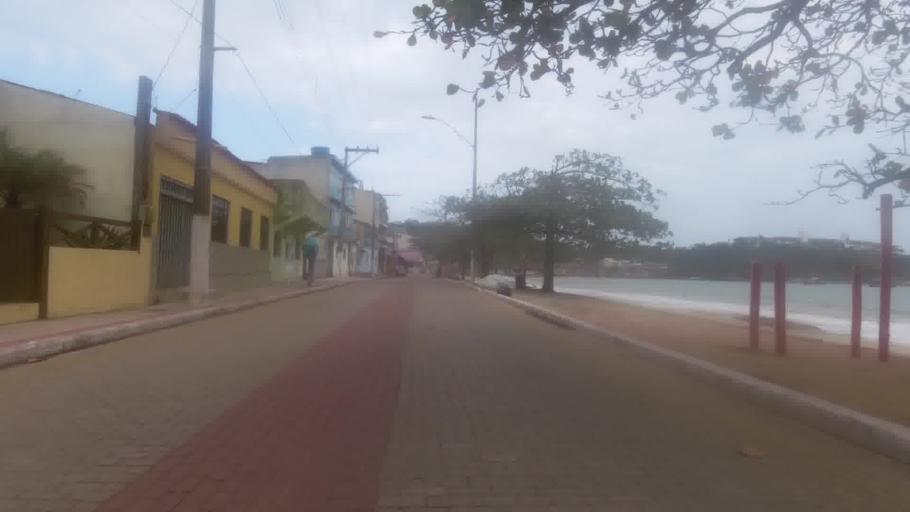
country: BR
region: Espirito Santo
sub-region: Piuma
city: Piuma
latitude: -20.8018
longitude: -40.5900
